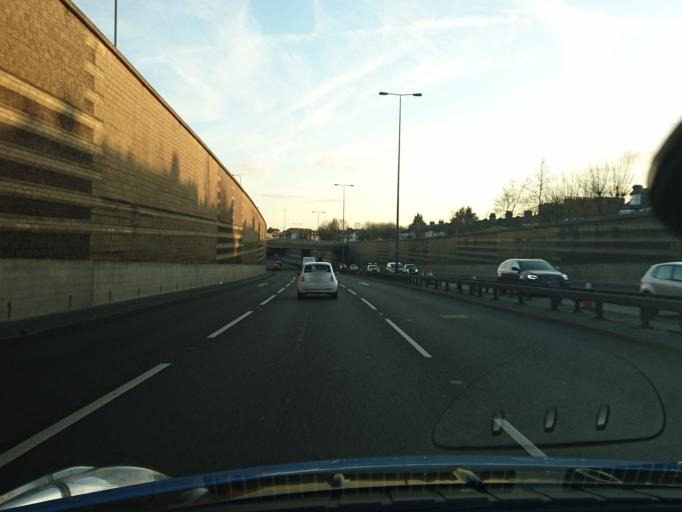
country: GB
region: England
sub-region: Greater London
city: Walthamstow
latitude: 51.5709
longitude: 0.0101
